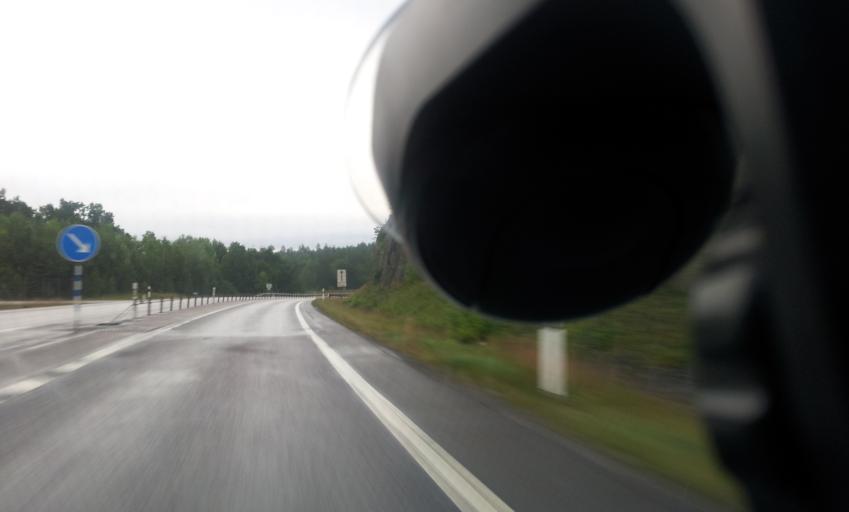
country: SE
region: Kalmar
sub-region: Vasterviks Kommun
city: Vaestervik
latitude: 57.7291
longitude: 16.5217
